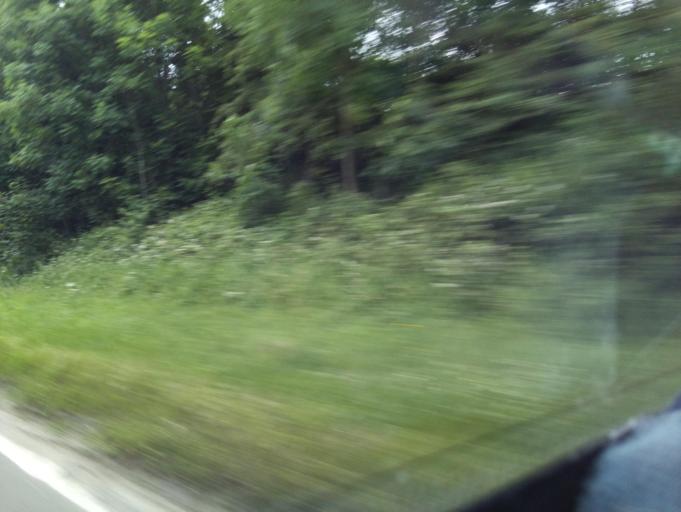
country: GB
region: England
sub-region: Derbyshire
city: Rodsley
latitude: 52.9230
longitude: -1.7619
